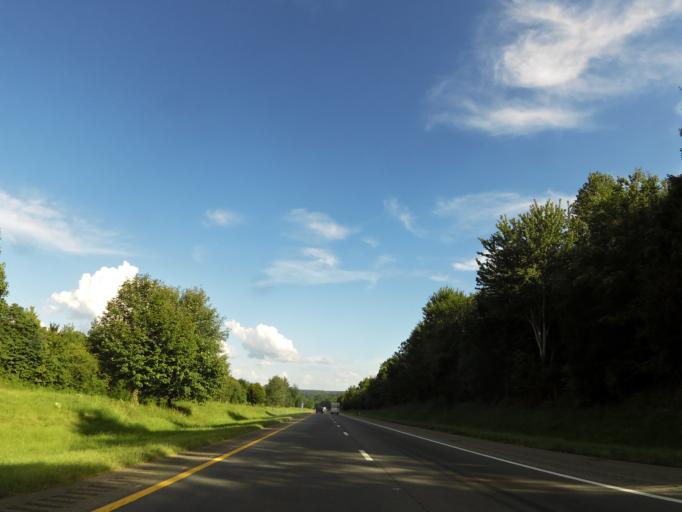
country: US
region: Tennessee
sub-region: Cheatham County
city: Pleasant View
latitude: 36.3834
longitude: -86.9952
